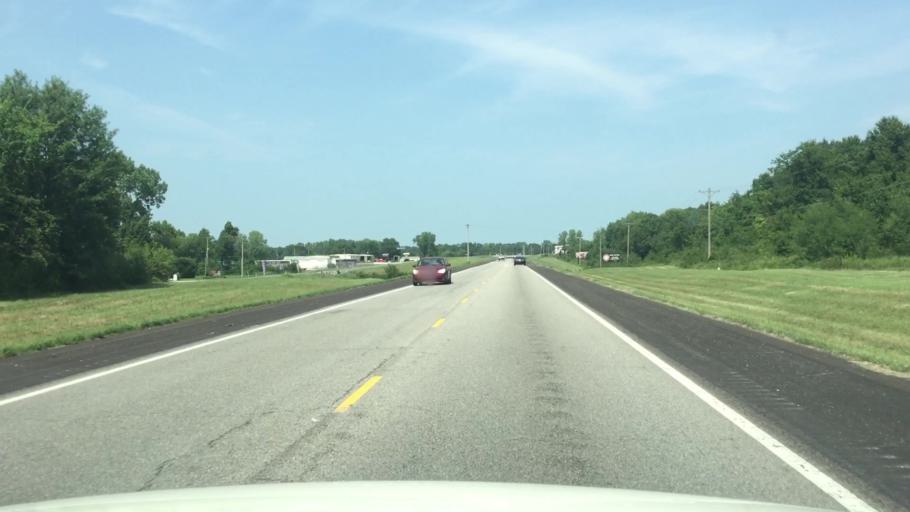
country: US
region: Kansas
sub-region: Crawford County
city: Pittsburg
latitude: 37.4309
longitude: -94.7130
